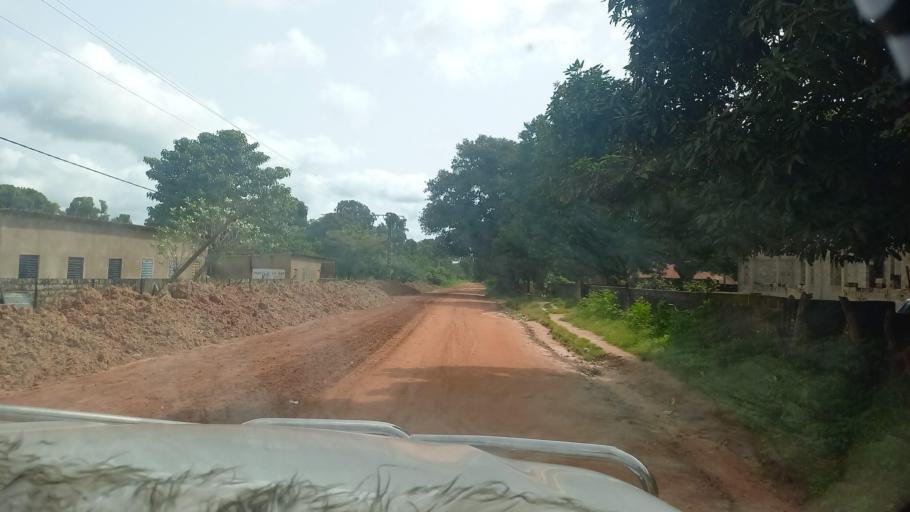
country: SN
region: Ziguinchor
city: Bignona
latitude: 12.7510
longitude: -16.2806
